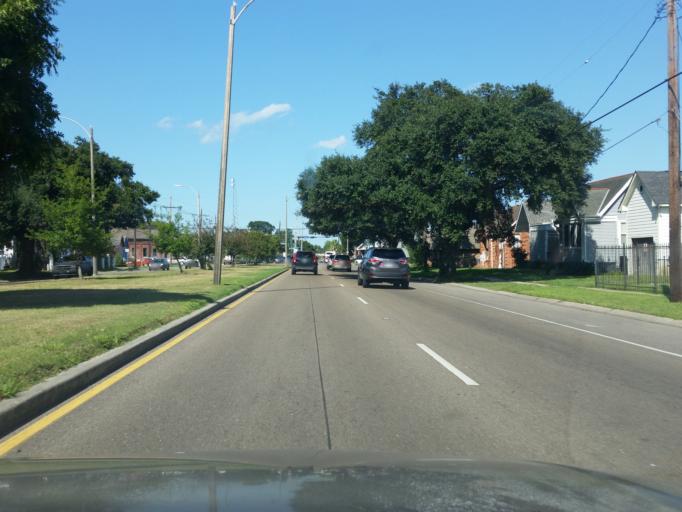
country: US
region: Louisiana
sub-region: Orleans Parish
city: New Orleans
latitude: 29.9865
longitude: -90.0689
